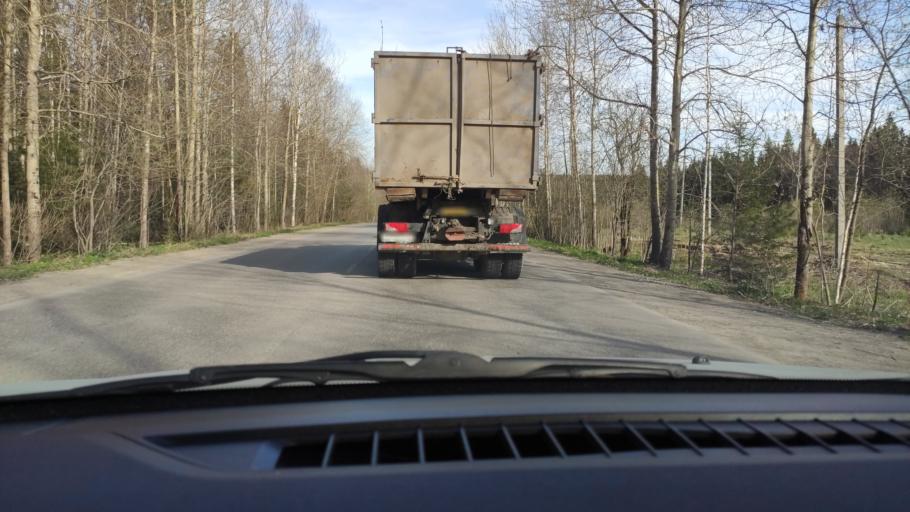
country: RU
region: Perm
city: Ferma
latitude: 57.9376
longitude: 56.4601
